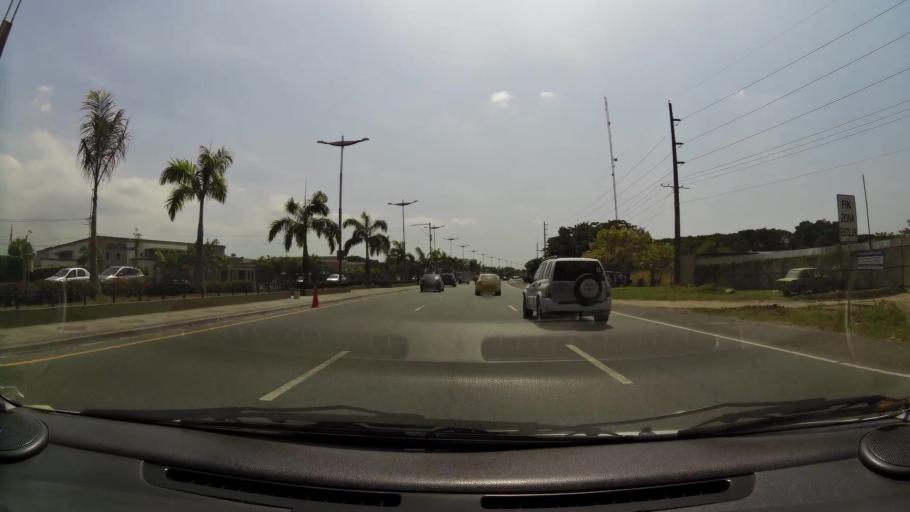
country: EC
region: Guayas
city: Eloy Alfaro
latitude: -2.1124
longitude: -79.8707
